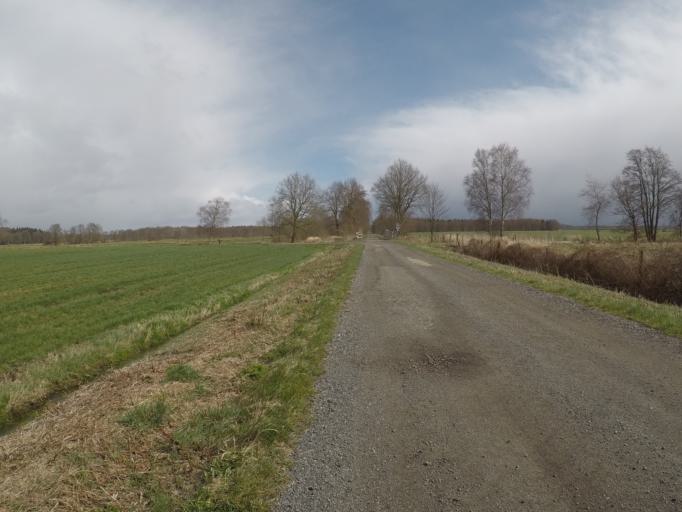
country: DE
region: Lower Saxony
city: Elmlohe
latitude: 53.6034
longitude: 8.6957
